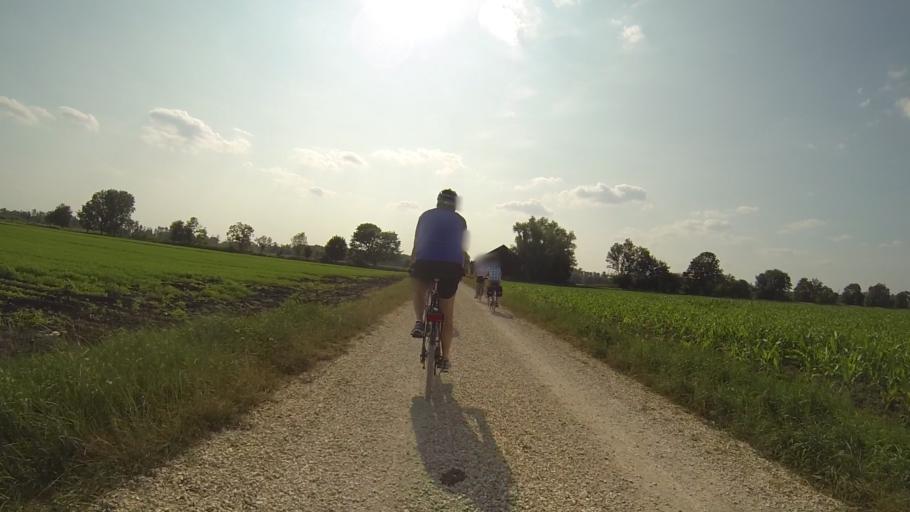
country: DE
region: Baden-Wuerttemberg
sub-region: Tuebingen Region
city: Rammingen
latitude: 48.4825
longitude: 10.1884
